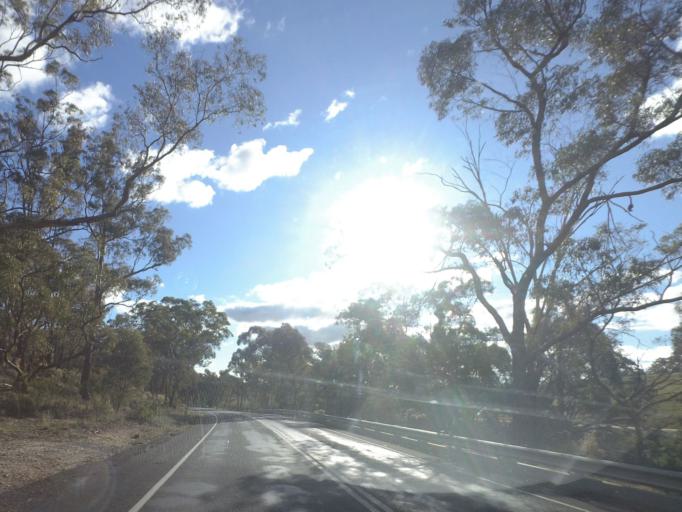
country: AU
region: Victoria
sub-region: Mount Alexander
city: Castlemaine
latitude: -37.1044
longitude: 144.3013
